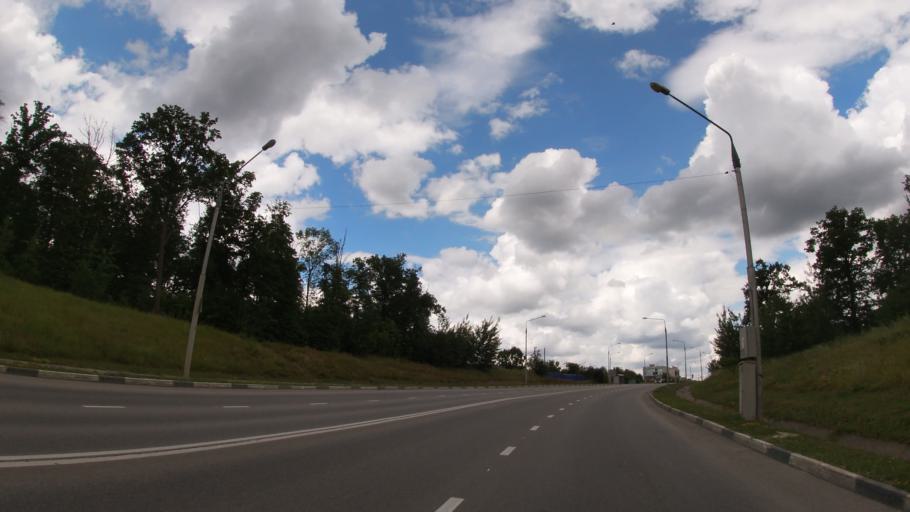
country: RU
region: Belgorod
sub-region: Belgorodskiy Rayon
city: Belgorod
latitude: 50.6242
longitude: 36.6114
